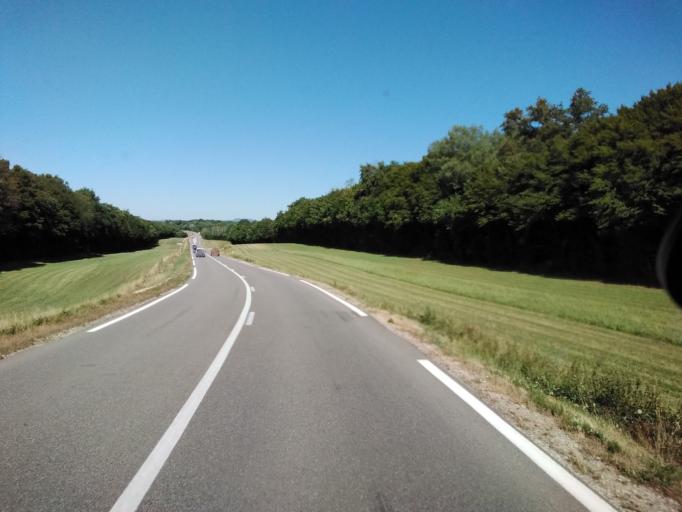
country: FR
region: Franche-Comte
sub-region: Departement du Jura
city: Poligny
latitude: 46.8325
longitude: 5.6084
